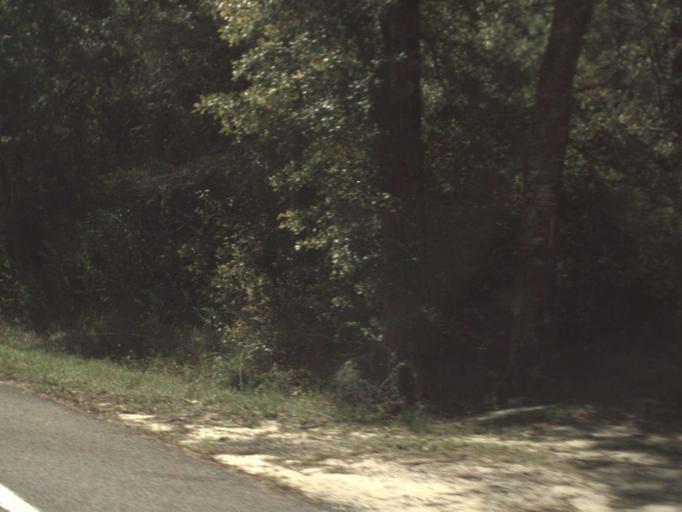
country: US
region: Florida
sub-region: Walton County
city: DeFuniak Springs
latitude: 30.9208
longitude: -86.1361
